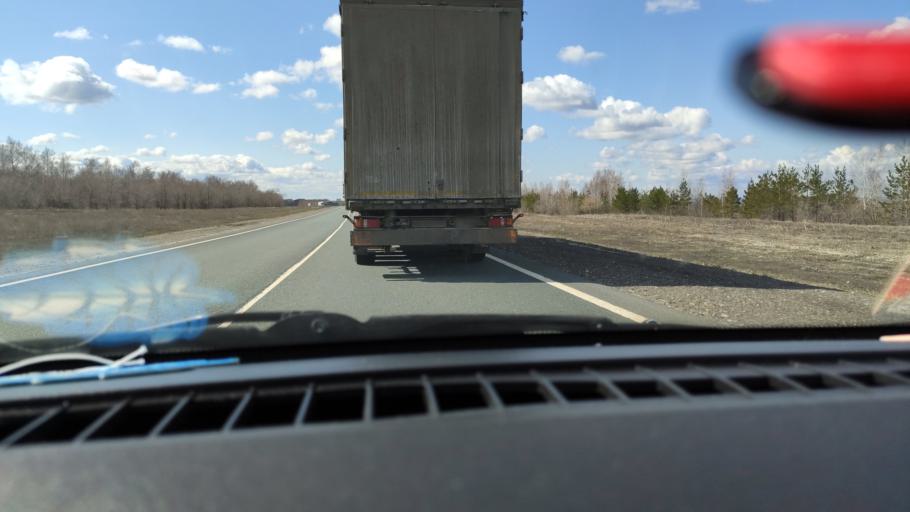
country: RU
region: Samara
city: Syzran'
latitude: 52.8576
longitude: 48.2615
